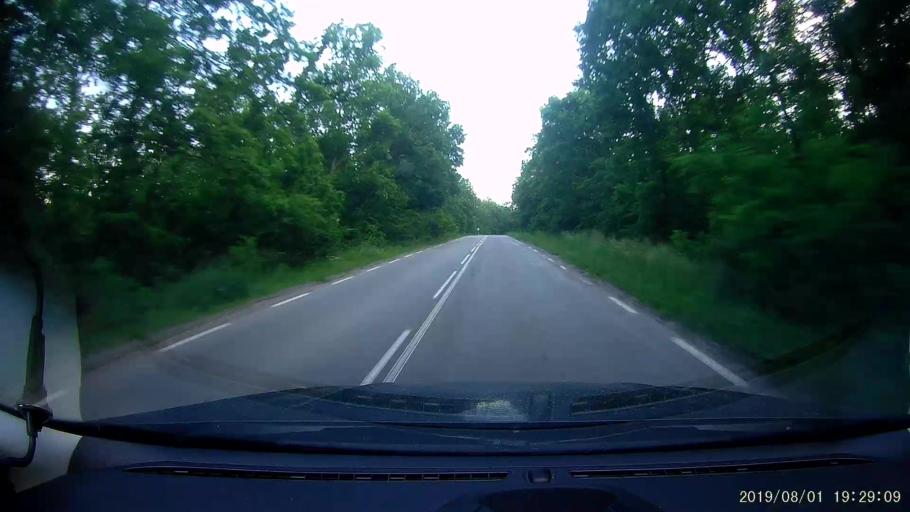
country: BG
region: Burgas
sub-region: Obshtina Sungurlare
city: Sungurlare
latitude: 42.8307
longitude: 26.9101
